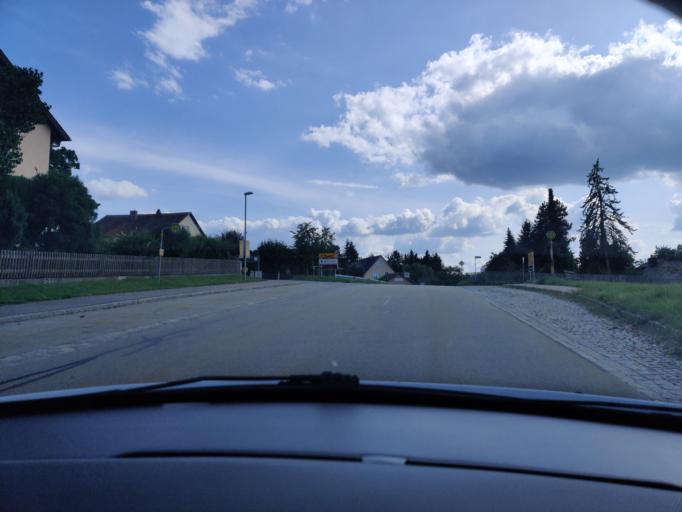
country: DE
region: Bavaria
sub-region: Upper Palatinate
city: Nabburg
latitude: 49.4678
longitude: 12.1876
